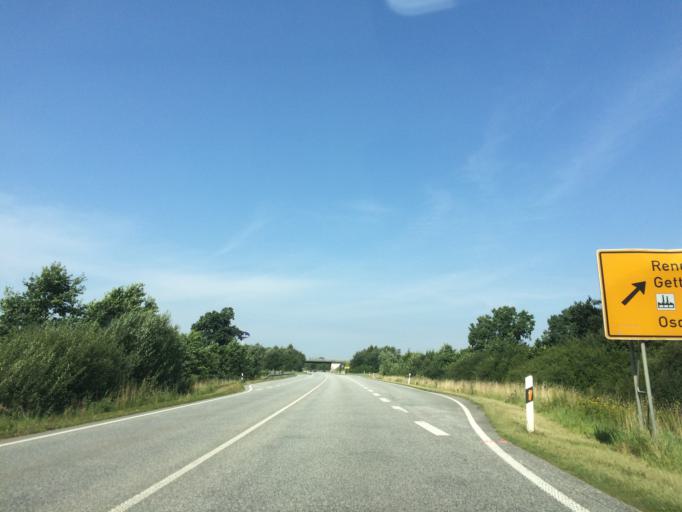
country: DE
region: Schleswig-Holstein
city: Tuttendorf
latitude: 54.4126
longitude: 9.9939
